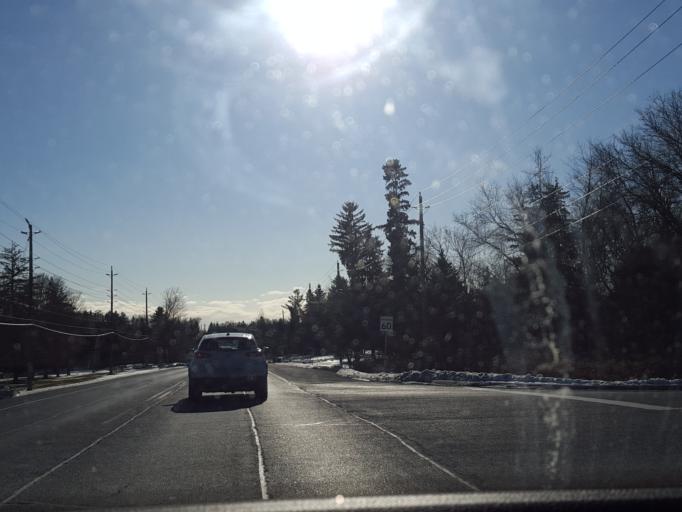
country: CA
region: Ontario
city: Ajax
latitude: 43.9367
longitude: -78.9606
